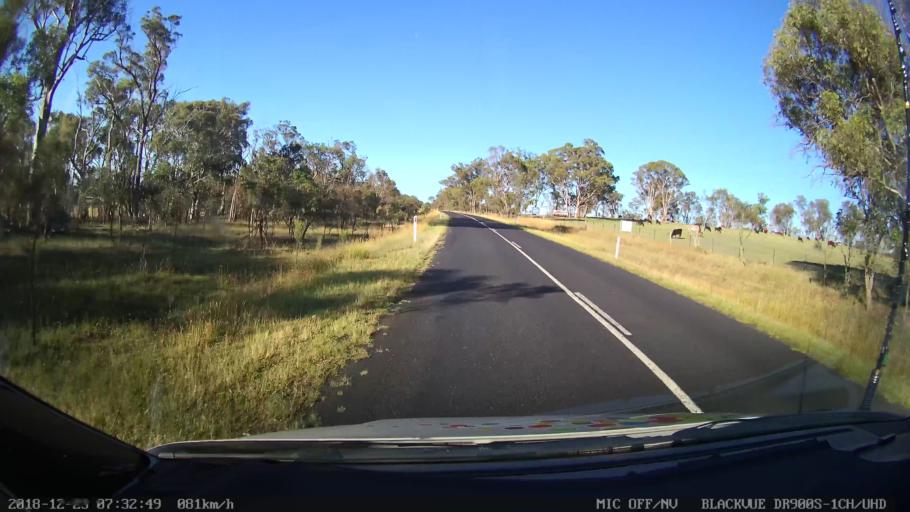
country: AU
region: New South Wales
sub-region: Armidale Dumaresq
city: Enmore
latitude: -30.5071
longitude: 152.1117
